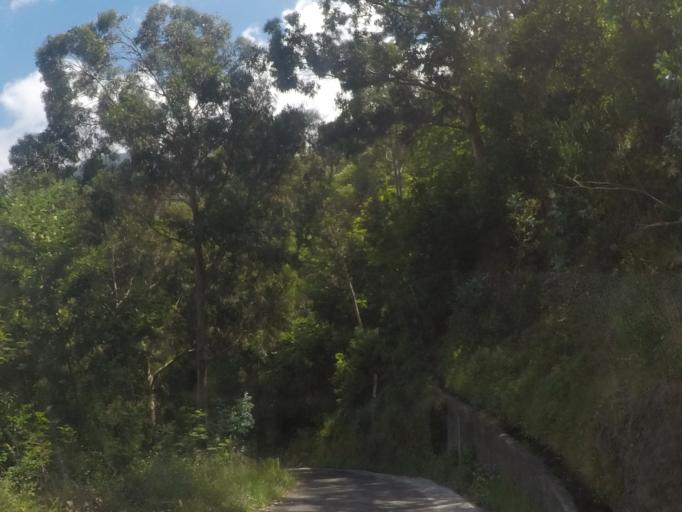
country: PT
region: Madeira
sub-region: Camara de Lobos
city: Curral das Freiras
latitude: 32.7138
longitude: -16.9730
